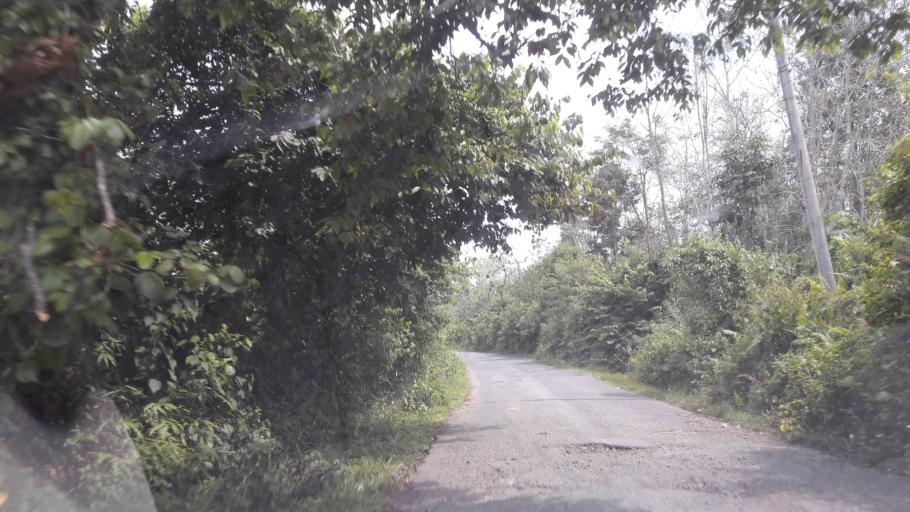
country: ID
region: South Sumatra
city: Gunungmenang
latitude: -3.1019
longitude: 103.8839
